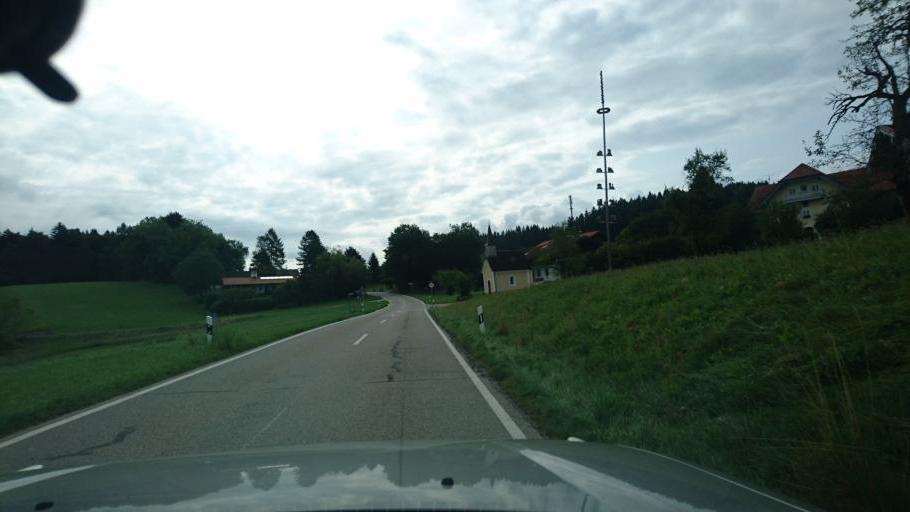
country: DE
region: Bavaria
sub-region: Upper Bavaria
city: Grabenstatt
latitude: 47.8346
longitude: 12.5615
